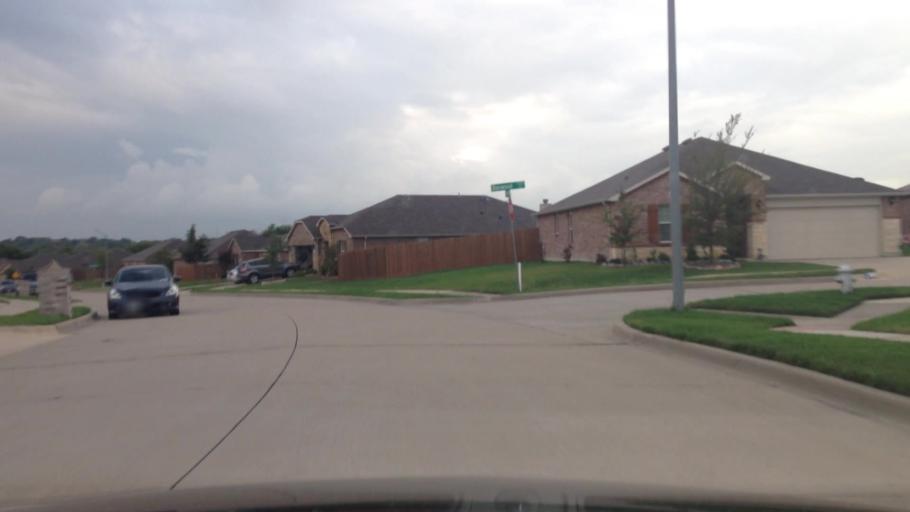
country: US
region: Texas
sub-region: Tarrant County
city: Crowley
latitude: 32.5663
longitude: -97.3395
